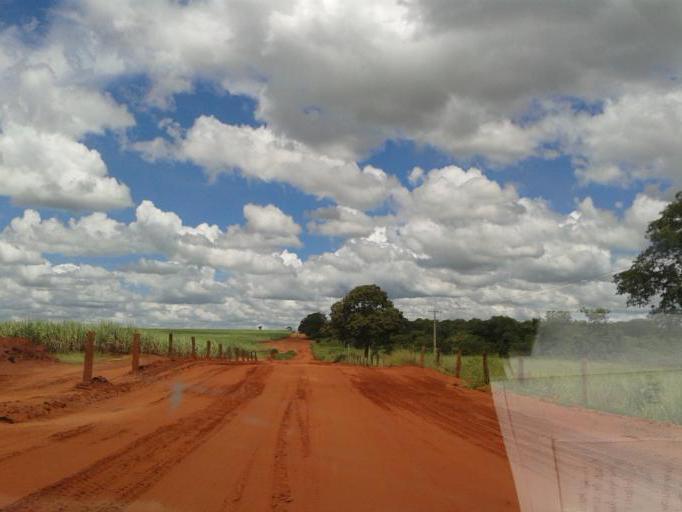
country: BR
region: Minas Gerais
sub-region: Santa Vitoria
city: Santa Vitoria
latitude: -18.8305
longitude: -50.0730
